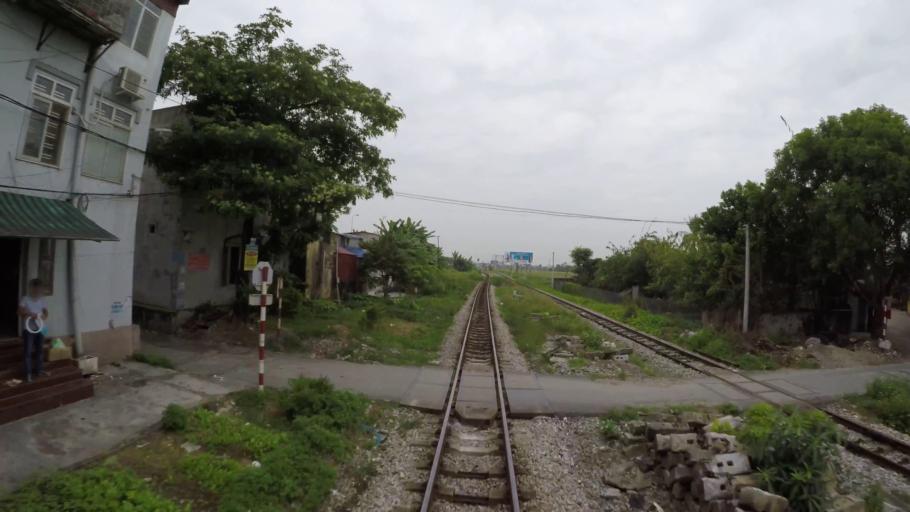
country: VN
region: Hai Duong
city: Phu Thai
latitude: 20.9322
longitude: 106.5526
